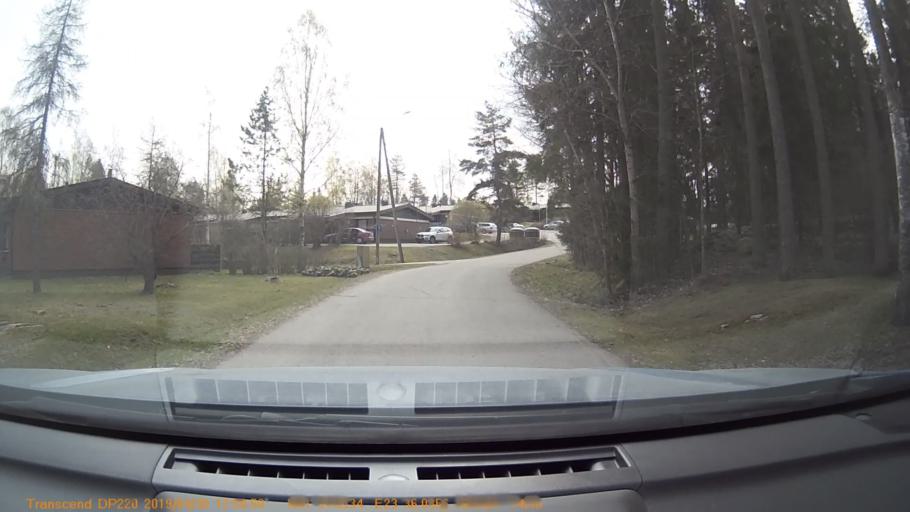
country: FI
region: Pirkanmaa
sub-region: Tampere
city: Yloejaervi
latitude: 61.5724
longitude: 23.6004
